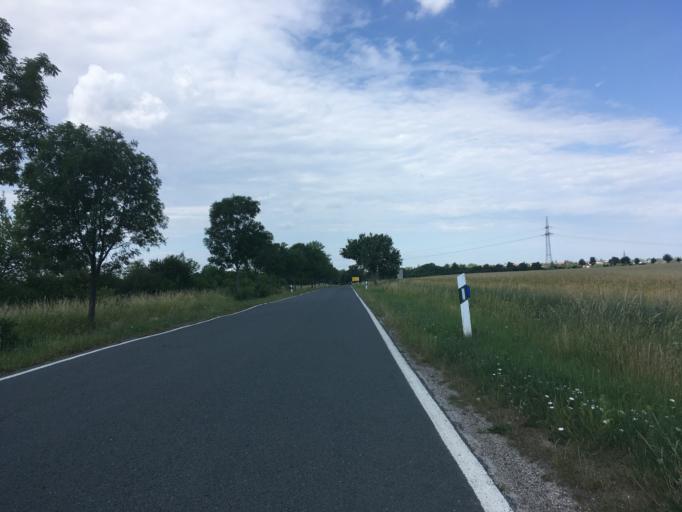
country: DE
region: Saxony-Anhalt
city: Baalberge
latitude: 51.7790
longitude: 11.7829
